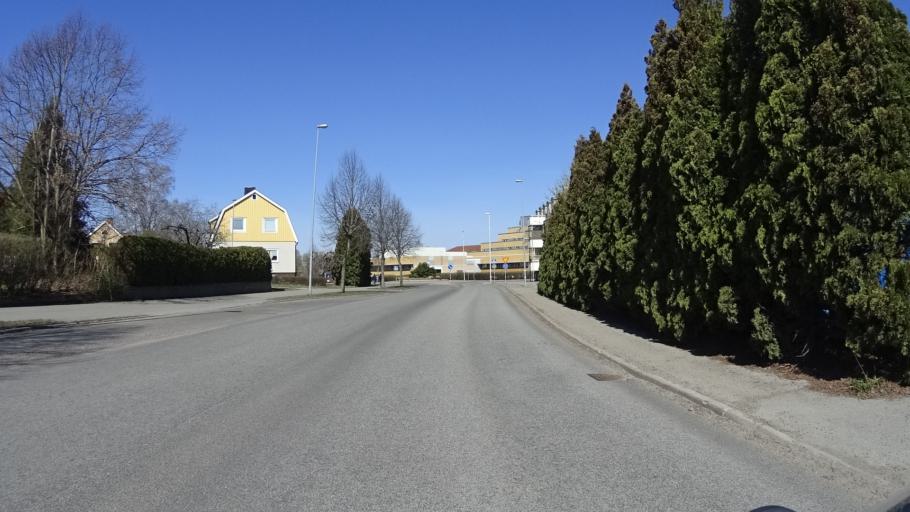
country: SE
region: Soedermanland
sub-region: Katrineholms Kommun
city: Katrineholm
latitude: 58.9898
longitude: 16.2224
